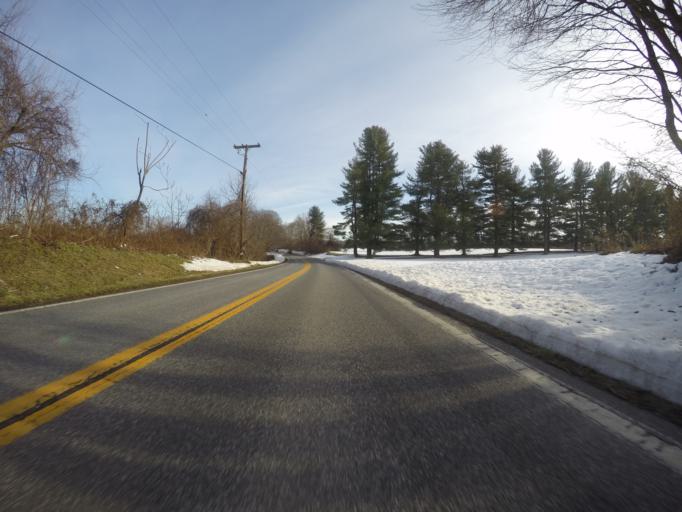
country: US
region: Maryland
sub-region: Baltimore County
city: Hunt Valley
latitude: 39.5418
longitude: -76.5571
